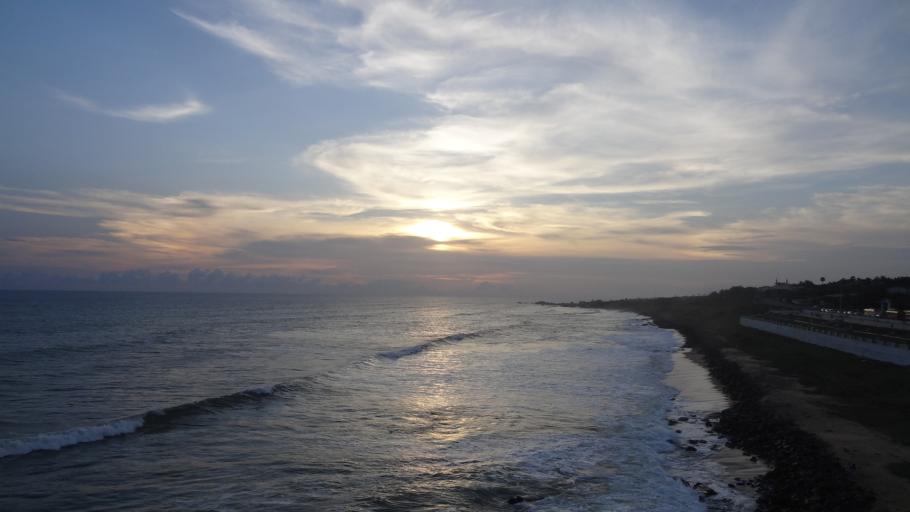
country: IN
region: Tamil Nadu
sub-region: Kanniyakumari
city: Kanniyakumari
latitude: 8.0781
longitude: 77.5462
